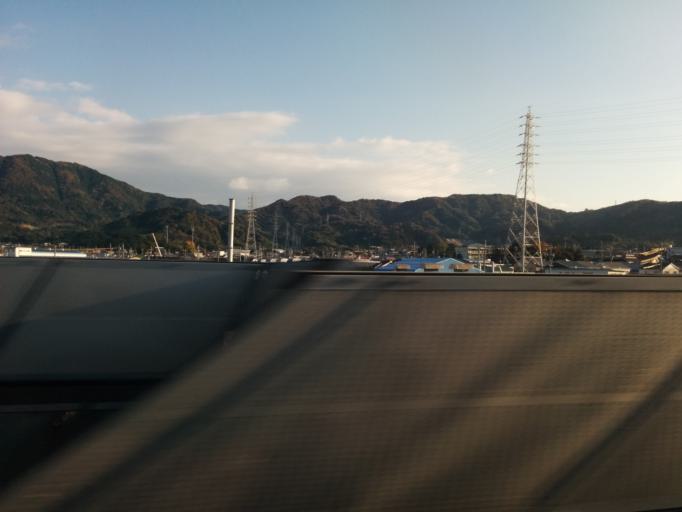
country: JP
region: Aichi
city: Gamagori
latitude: 34.8234
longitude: 137.2454
